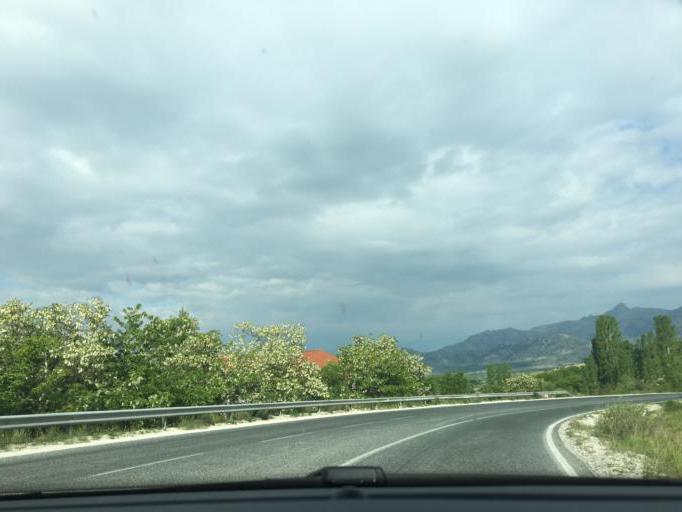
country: MK
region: Prilep
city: Prilep
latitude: 41.3670
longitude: 21.6433
